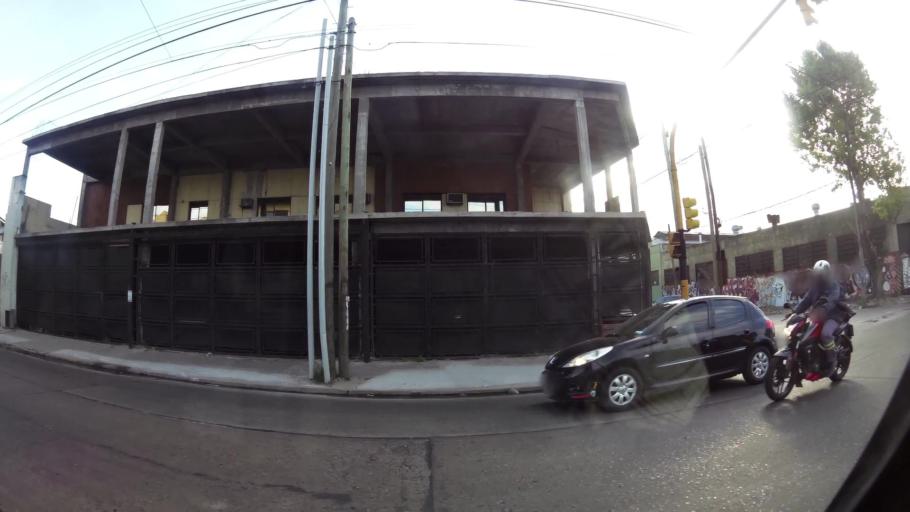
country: AR
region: Buenos Aires
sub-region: Partido de Avellaneda
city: Avellaneda
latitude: -34.6881
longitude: -58.3567
